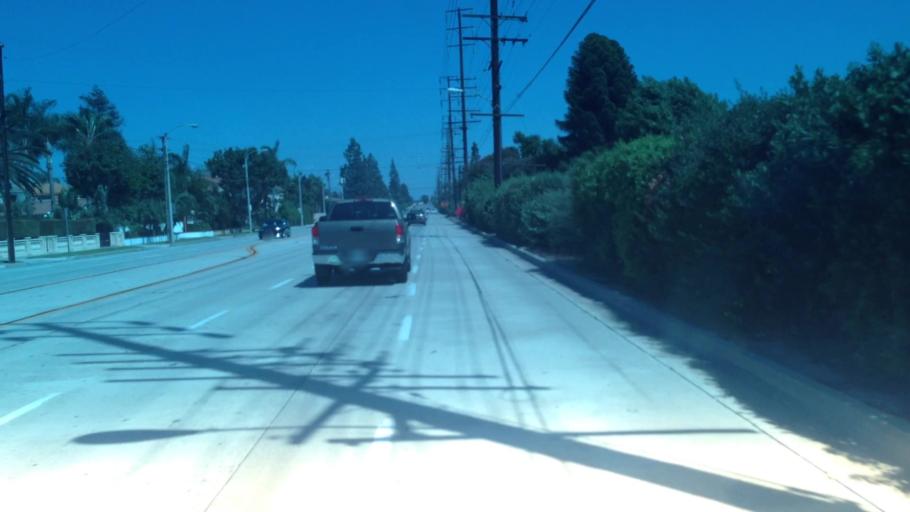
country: US
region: California
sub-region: Los Angeles County
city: Downey
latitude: 33.9434
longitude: -118.1093
